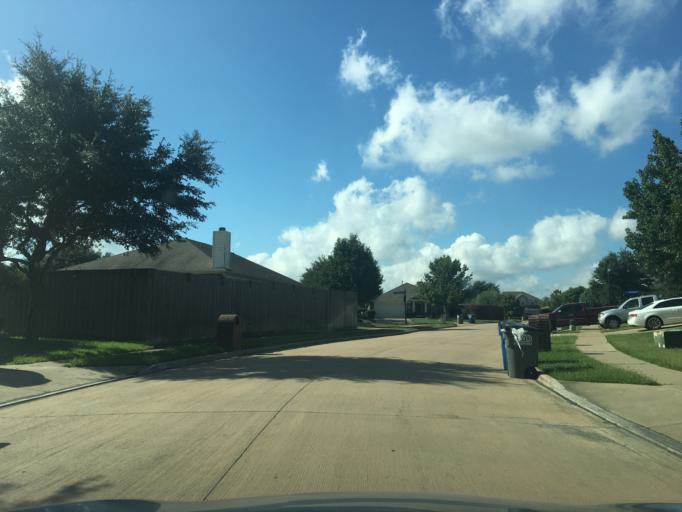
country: US
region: Texas
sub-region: Dallas County
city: Sachse
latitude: 32.9663
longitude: -96.5758
